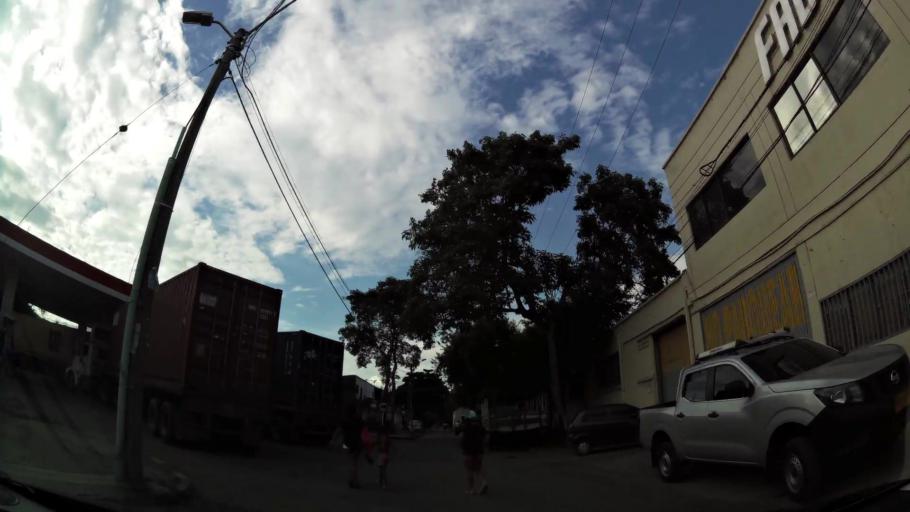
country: CO
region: Valle del Cauca
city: Cali
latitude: 3.4542
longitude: -76.5096
